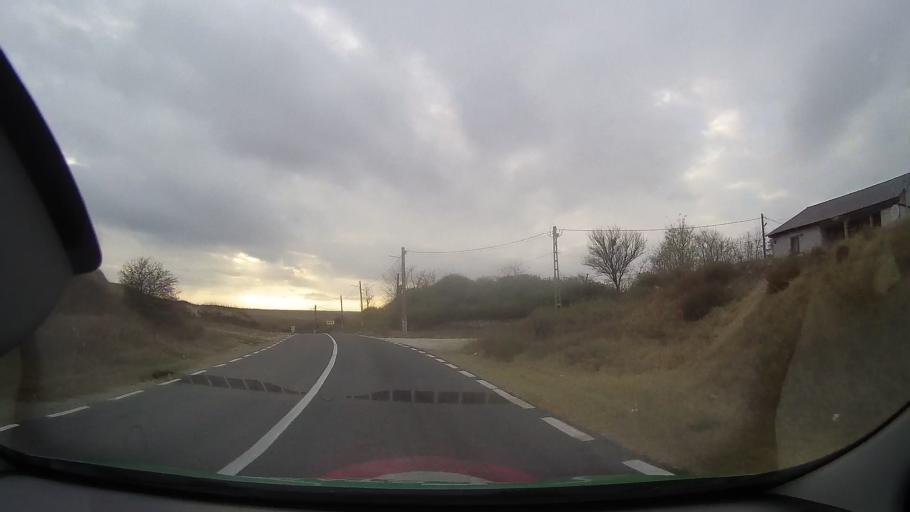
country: RO
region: Constanta
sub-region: Comuna Deleni
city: Deleni
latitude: 44.0928
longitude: 28.0144
